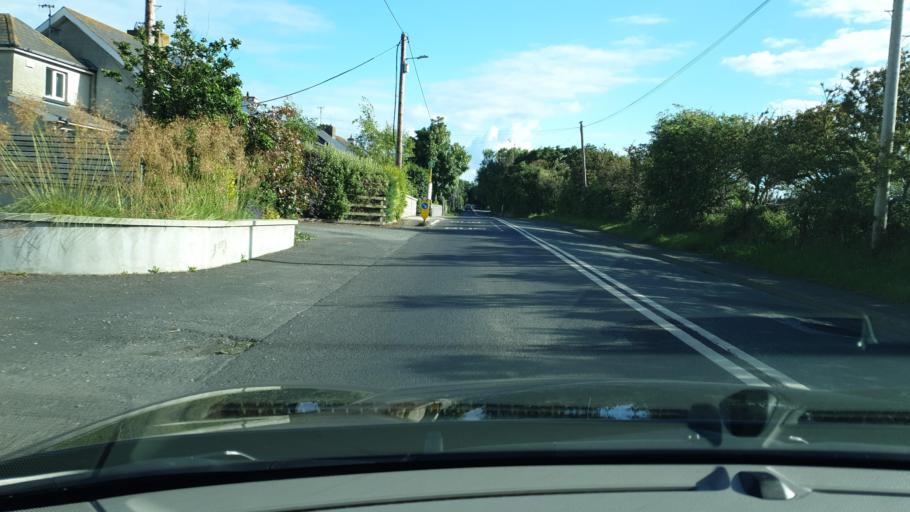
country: IE
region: Leinster
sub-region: Fingal County
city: Skerries
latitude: 53.5672
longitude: -6.1021
